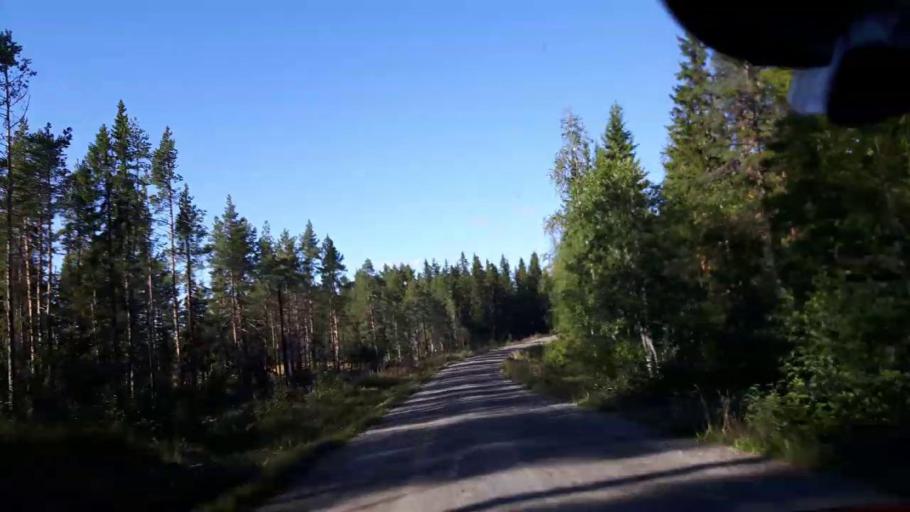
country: SE
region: Jaemtland
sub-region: Ragunda Kommun
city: Hammarstrand
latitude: 63.5228
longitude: 16.0559
